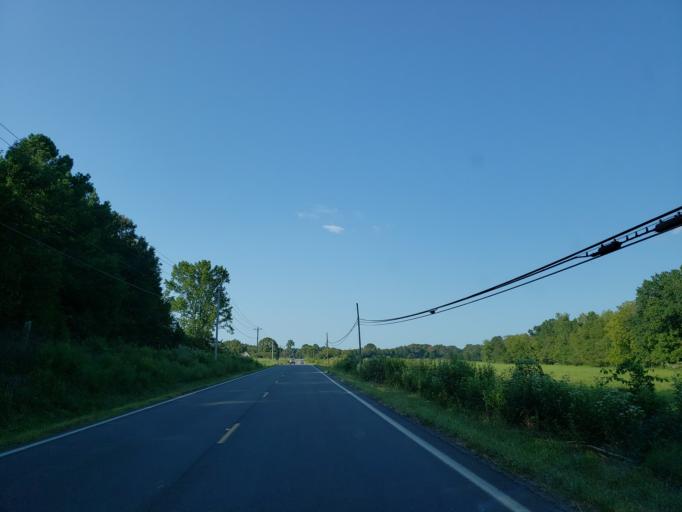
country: US
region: Tennessee
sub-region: Bradley County
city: Wildwood Lake
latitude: 35.0163
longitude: -84.7333
